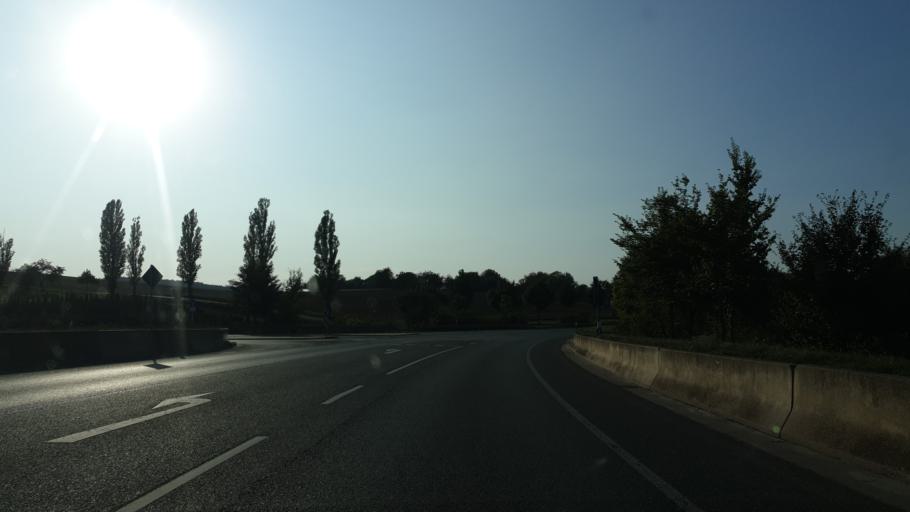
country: DE
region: Thuringia
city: Bad Kostritz
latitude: 50.9365
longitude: 12.0029
